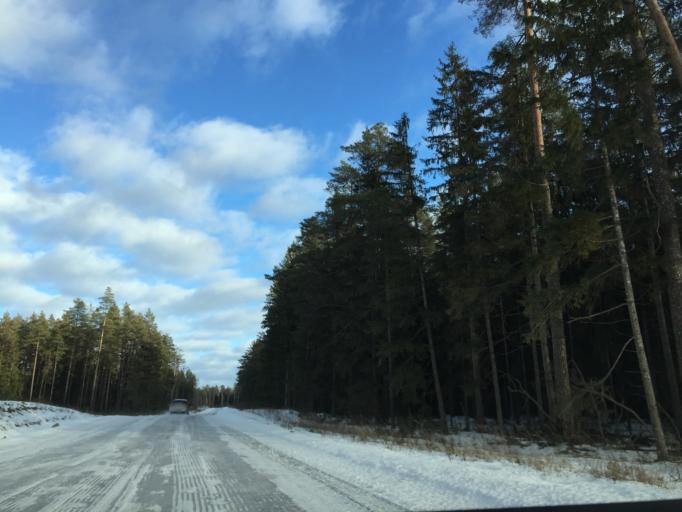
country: LV
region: Ogre
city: Jumprava
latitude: 56.5876
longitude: 24.9692
